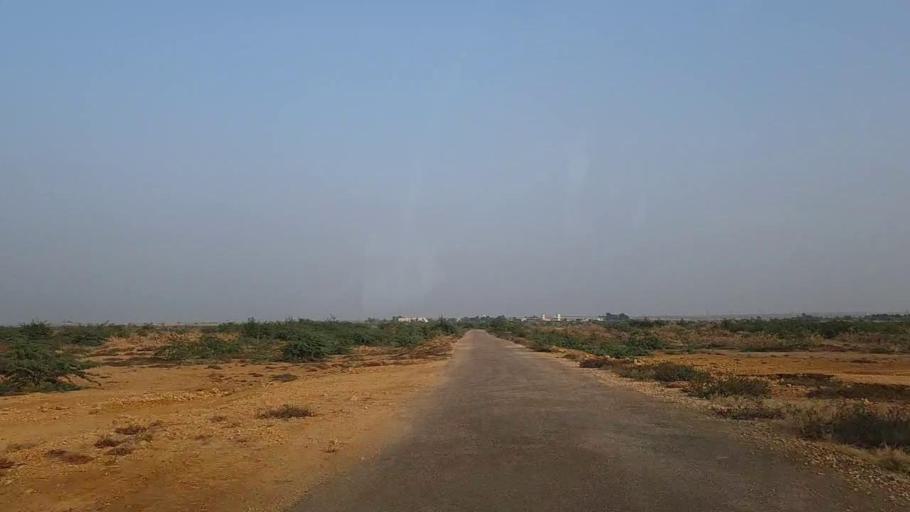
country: PK
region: Sindh
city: Thatta
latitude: 24.6905
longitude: 67.8365
